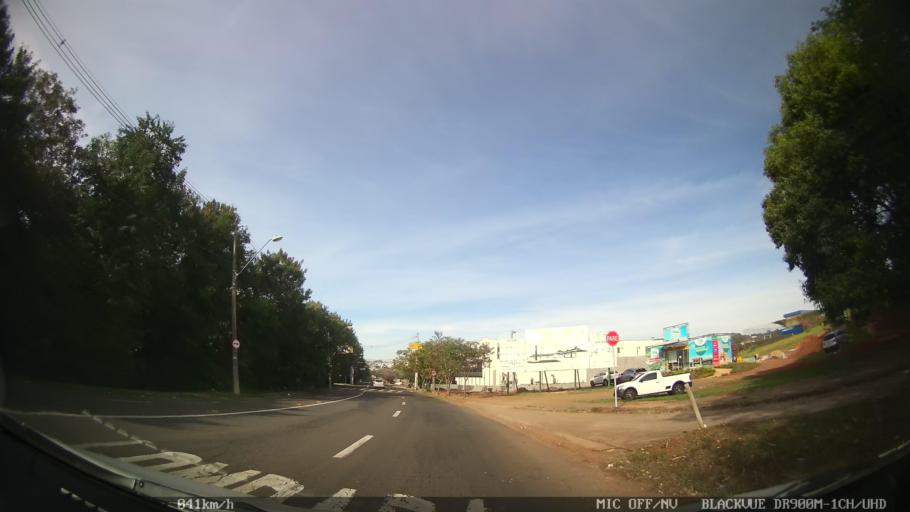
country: BR
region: Sao Paulo
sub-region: Piracicaba
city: Piracicaba
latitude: -22.7271
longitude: -47.6726
